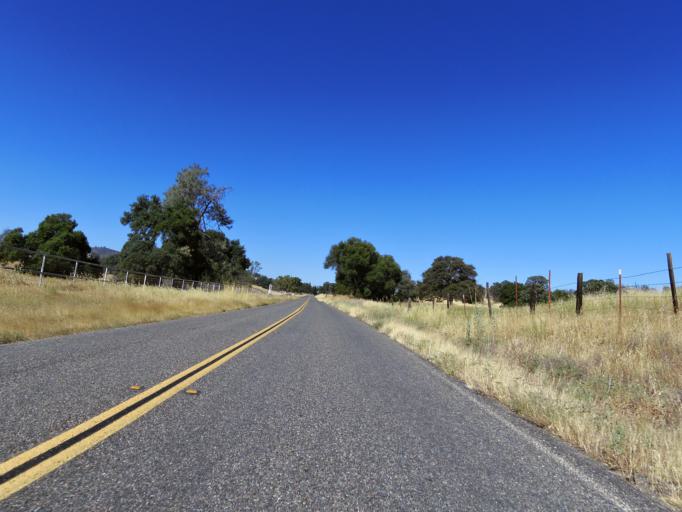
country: US
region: California
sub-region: Mariposa County
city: Mariposa
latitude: 37.4764
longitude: -120.1180
